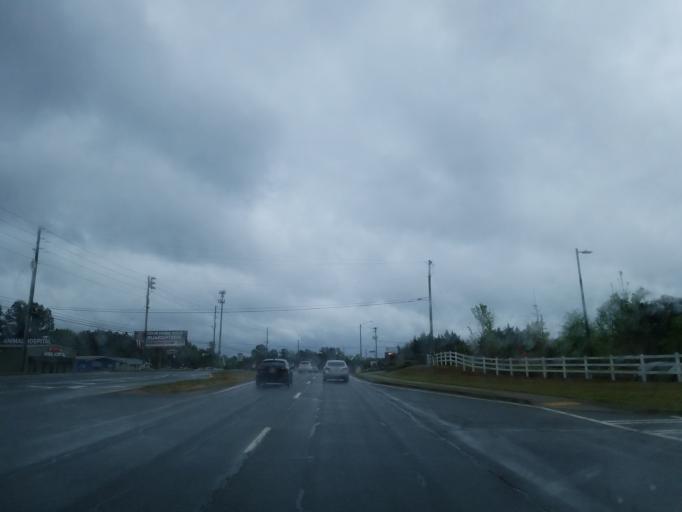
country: US
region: Georgia
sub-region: Cherokee County
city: Woodstock
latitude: 34.0846
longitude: -84.5590
